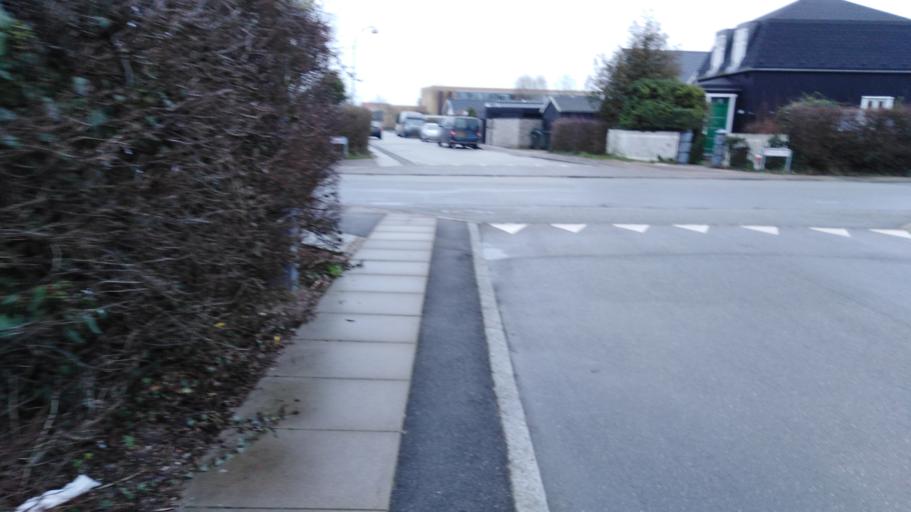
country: DK
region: Capital Region
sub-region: Hvidovre Kommune
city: Hvidovre
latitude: 55.6202
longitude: 12.4863
